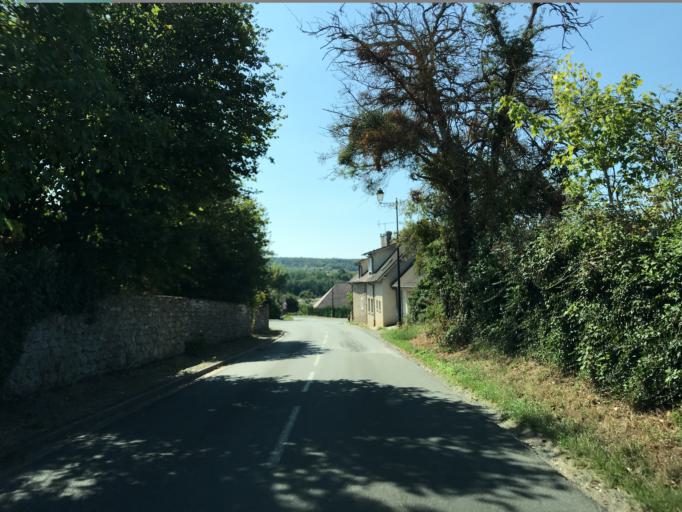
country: FR
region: Haute-Normandie
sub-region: Departement de l'Eure
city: Houlbec-Cocherel
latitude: 49.0772
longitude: 1.3055
